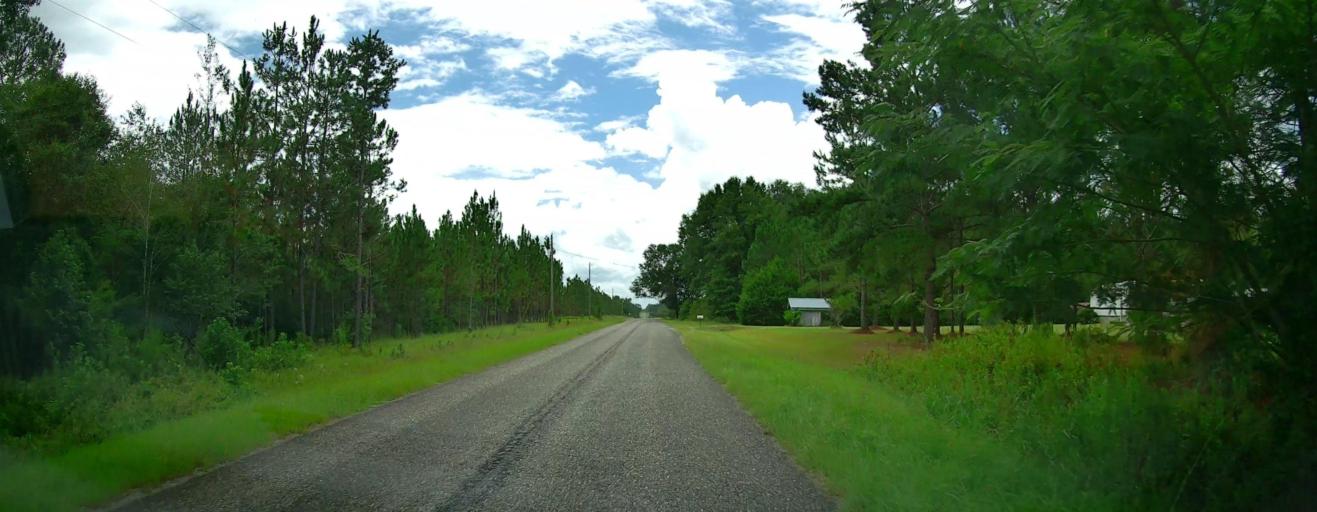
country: US
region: Georgia
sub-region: Dooly County
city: Vienna
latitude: 32.0616
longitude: -83.6277
